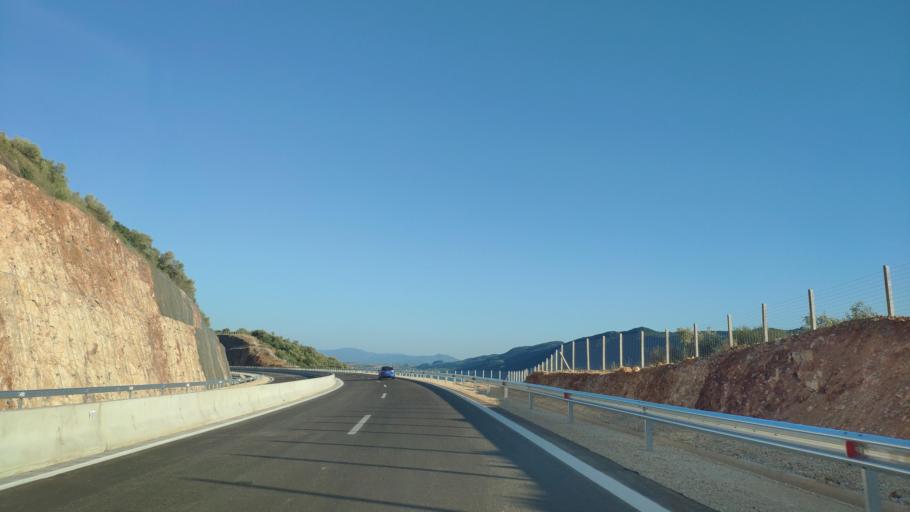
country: GR
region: West Greece
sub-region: Nomos Aitolias kai Akarnanias
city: Stanos
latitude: 38.7740
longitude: 21.1569
